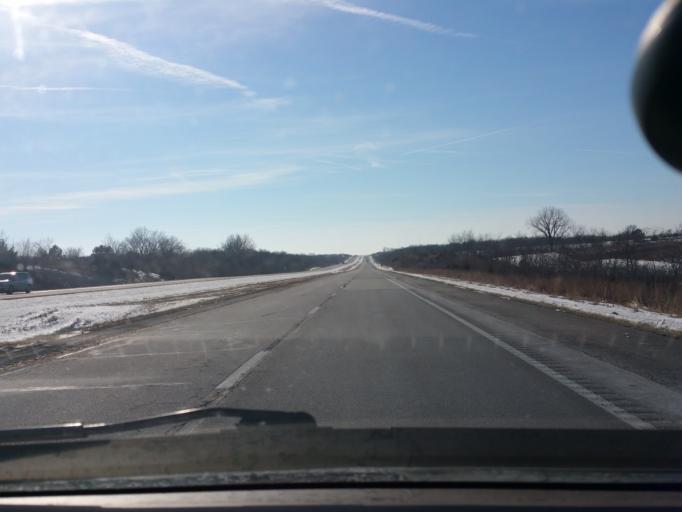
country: US
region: Missouri
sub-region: Harrison County
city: Bethany
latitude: 40.4141
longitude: -93.9920
